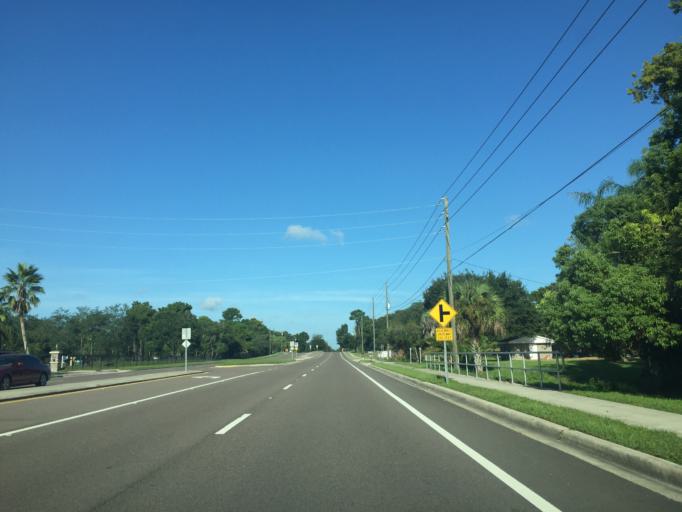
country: US
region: Florida
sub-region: Seminole County
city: Winter Springs
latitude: 28.6702
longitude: -81.2899
